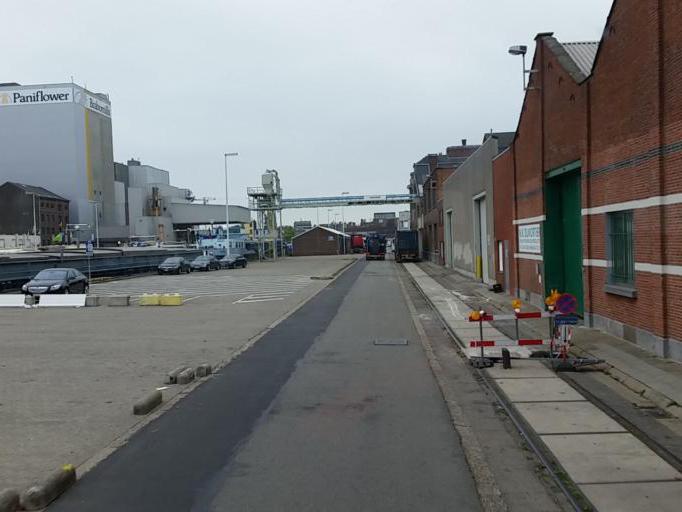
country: BE
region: Flanders
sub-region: Provincie Antwerpen
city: Antwerpen
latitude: 51.2408
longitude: 4.4497
